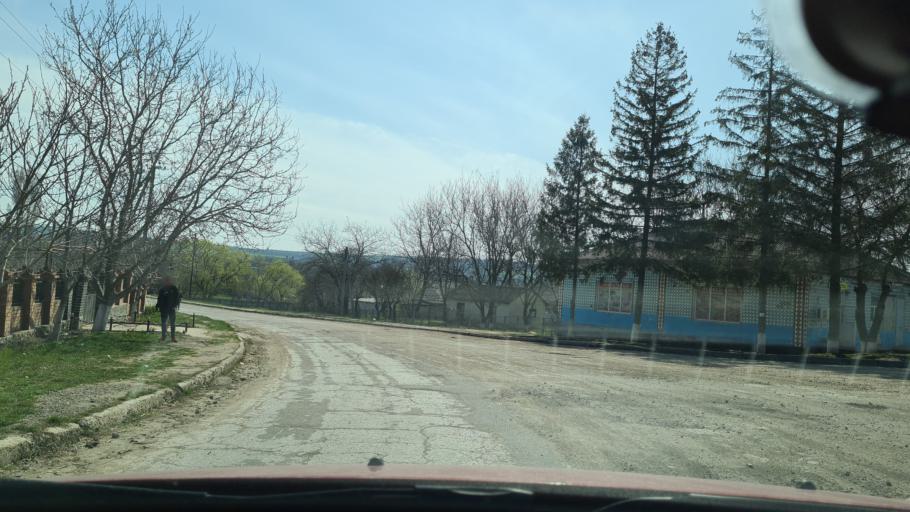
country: MD
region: Ungheni
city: Ungheni
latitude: 47.2692
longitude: 27.9305
